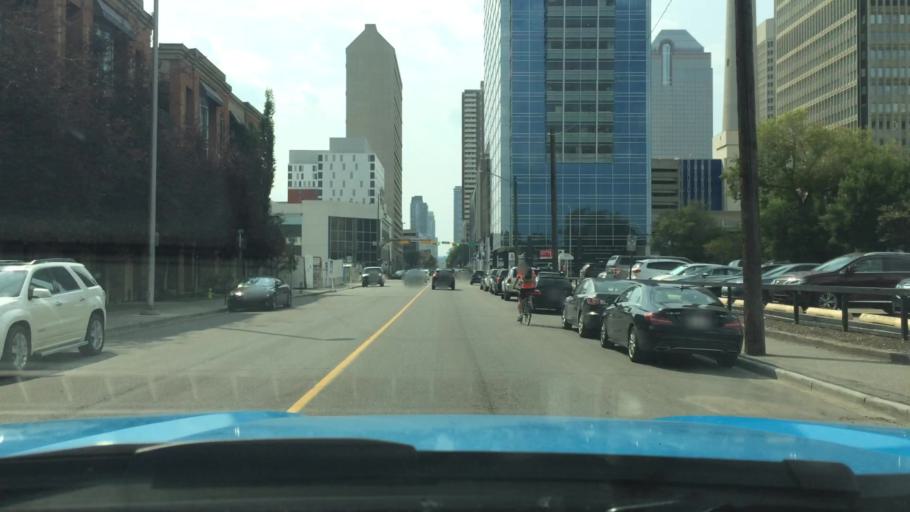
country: CA
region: Alberta
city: Calgary
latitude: 51.0432
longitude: -114.0587
